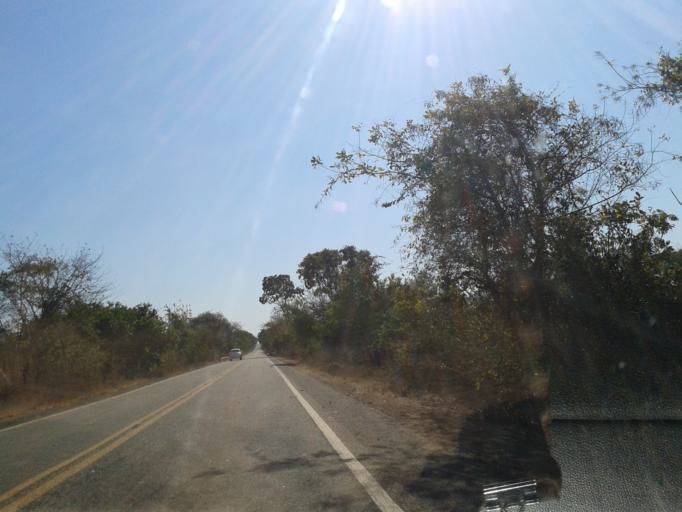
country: BR
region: Goias
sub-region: Mozarlandia
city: Mozarlandia
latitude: -14.4909
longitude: -50.4822
